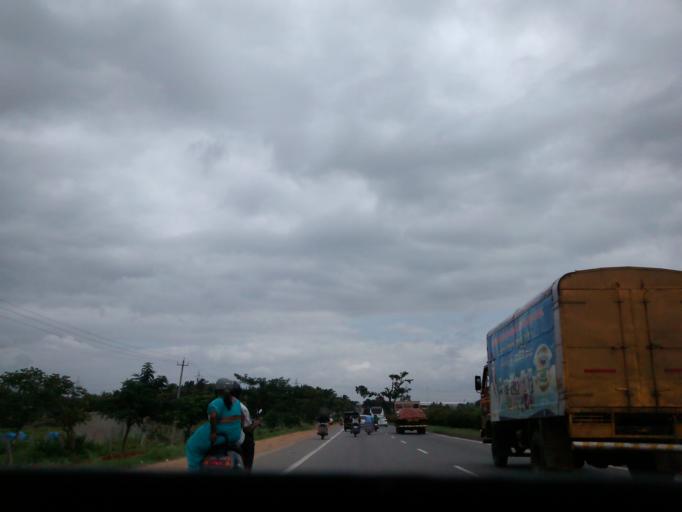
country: IN
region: Karnataka
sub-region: Bangalore Rural
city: Nelamangala
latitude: 13.1263
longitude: 77.3634
